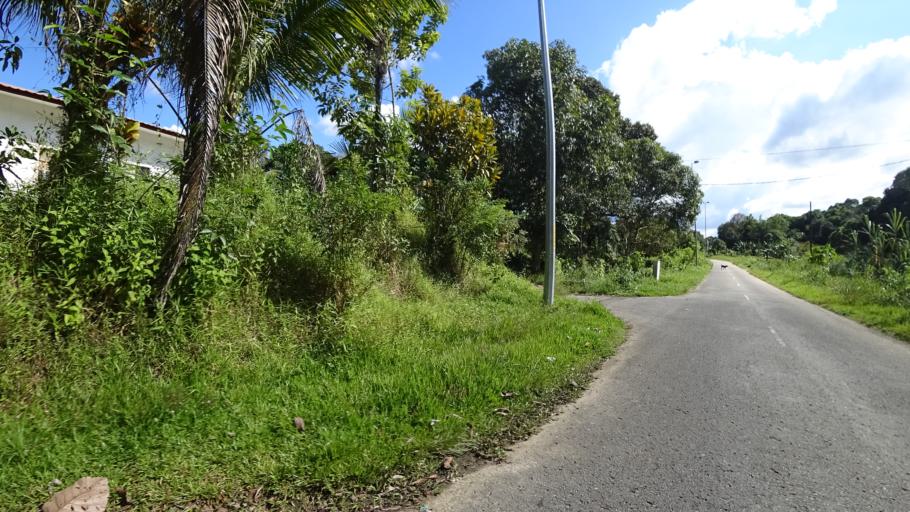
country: BN
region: Tutong
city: Tutong
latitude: 4.7373
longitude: 114.7909
